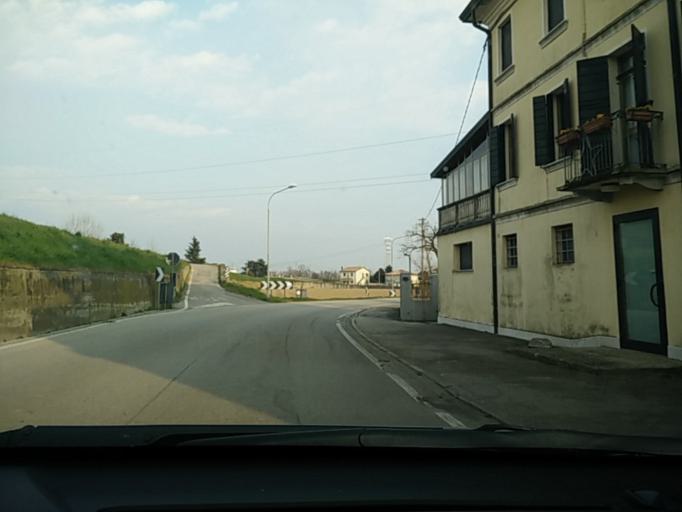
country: IT
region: Veneto
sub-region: Provincia di Treviso
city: Ponte di Piave
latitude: 45.7057
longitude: 12.4527
